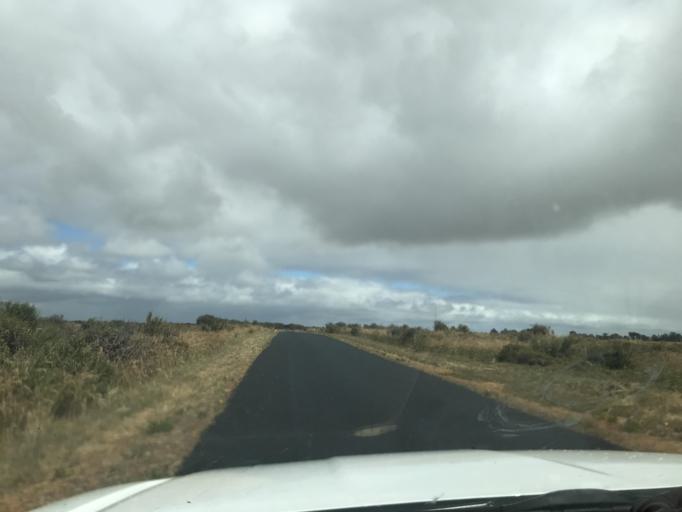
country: AU
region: South Australia
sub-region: Tatiara
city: Bordertown
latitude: -36.1350
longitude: 141.1813
